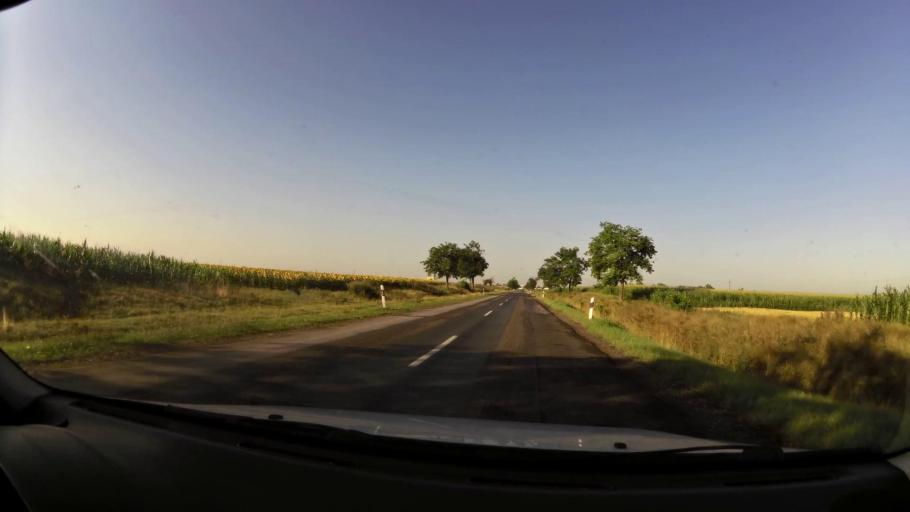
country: HU
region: Pest
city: Cegled
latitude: 47.2058
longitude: 19.8191
